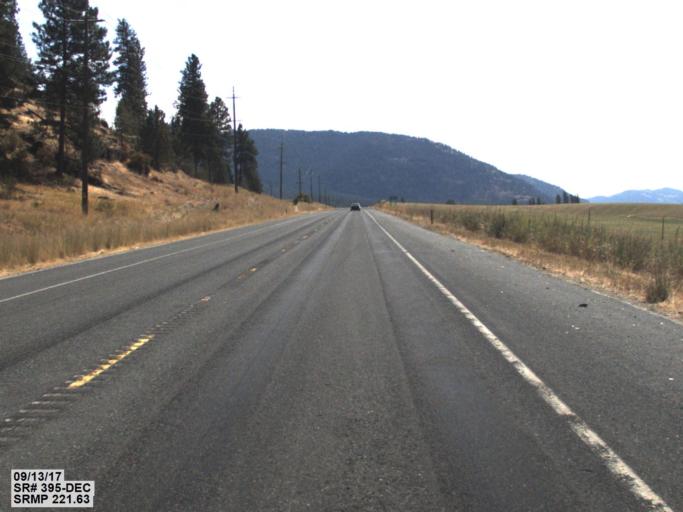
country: US
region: Washington
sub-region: Stevens County
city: Colville
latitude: 48.4379
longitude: -117.8647
